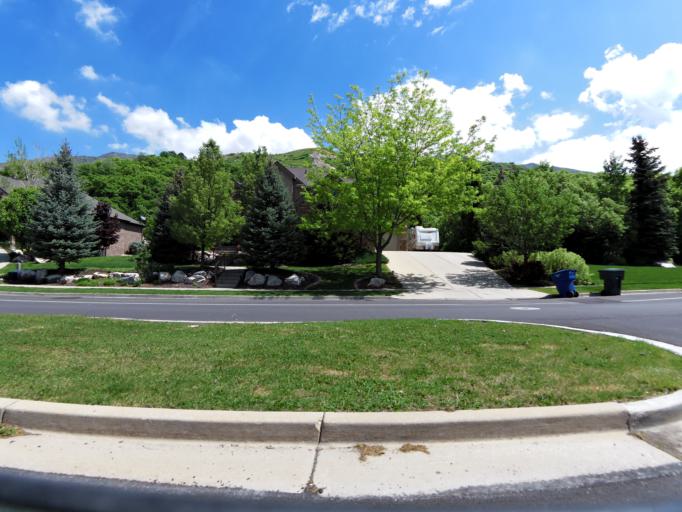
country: US
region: Utah
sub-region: Weber County
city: Uintah
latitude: 41.1661
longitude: -111.9262
